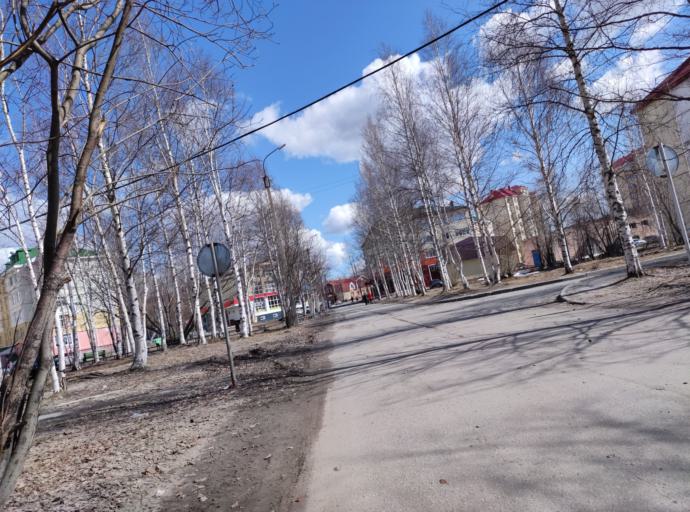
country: RU
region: Khanty-Mansiyskiy Avtonomnyy Okrug
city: Langepas
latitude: 61.2529
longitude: 75.1693
